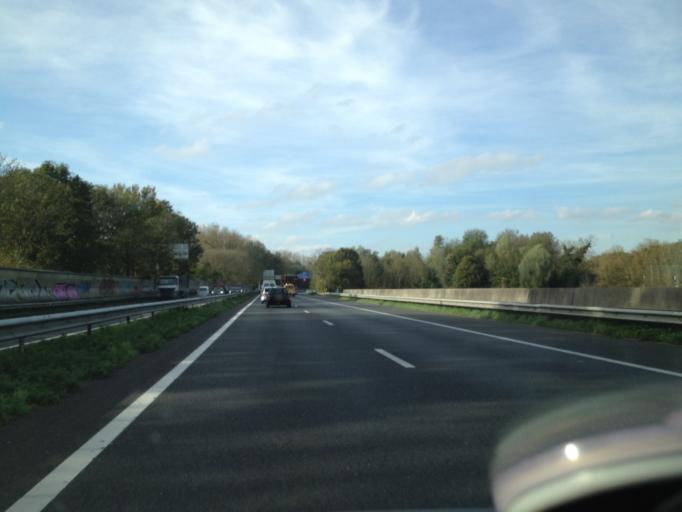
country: NL
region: Limburg
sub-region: Gemeente Nuth
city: Nuth
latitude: 50.9144
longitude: 5.9017
